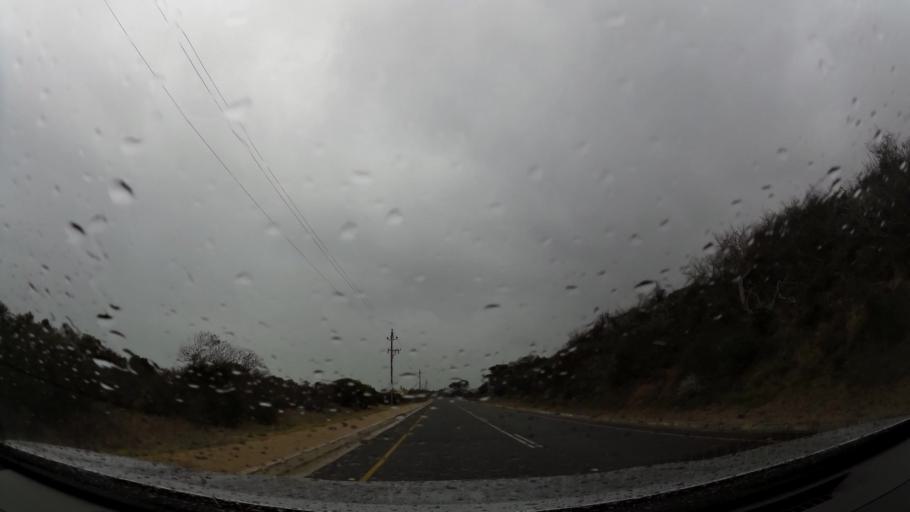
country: ZA
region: Western Cape
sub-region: Eden District Municipality
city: Mossel Bay
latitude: -34.0492
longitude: 22.2767
